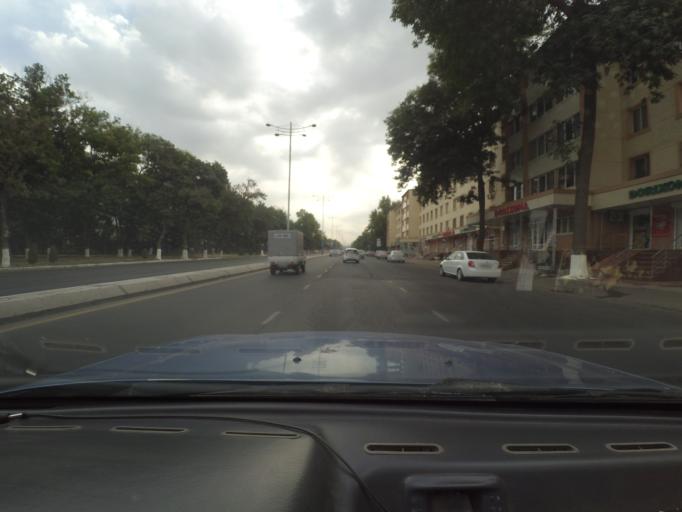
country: UZ
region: Toshkent
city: Salor
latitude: 41.3551
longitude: 69.3581
